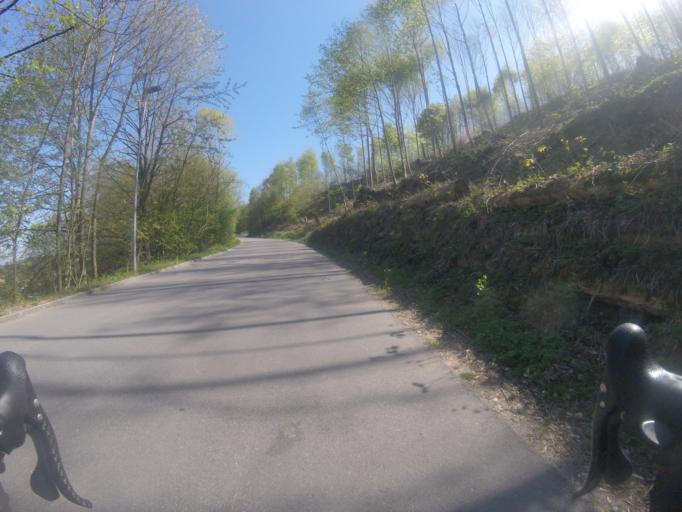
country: CH
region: Bern
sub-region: Bern-Mittelland District
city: Laupen
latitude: 46.9035
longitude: 7.2419
